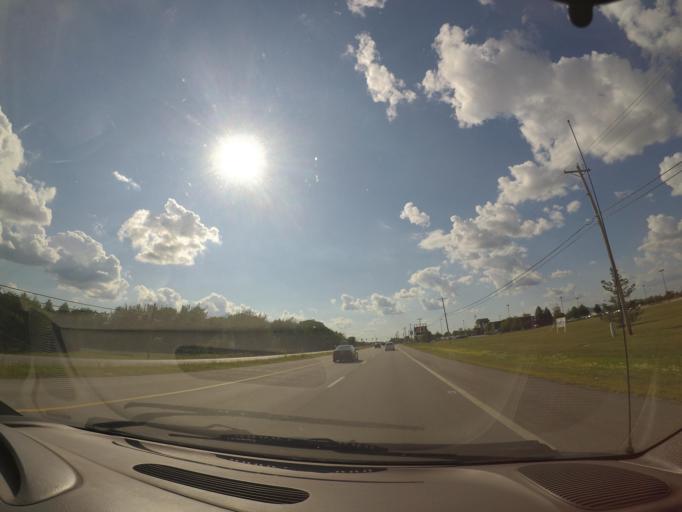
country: US
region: Ohio
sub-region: Wood County
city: Perrysburg
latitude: 41.5423
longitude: -83.5839
